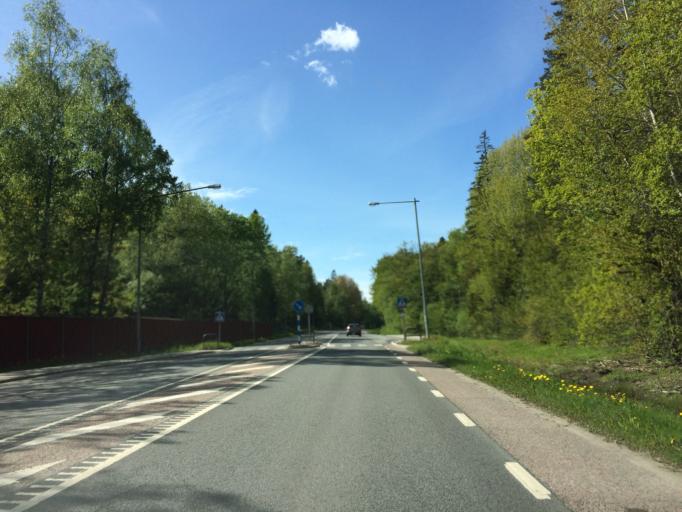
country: SE
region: Stockholm
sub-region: Norrtalje Kommun
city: Bergshamra
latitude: 59.4162
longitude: 18.0139
